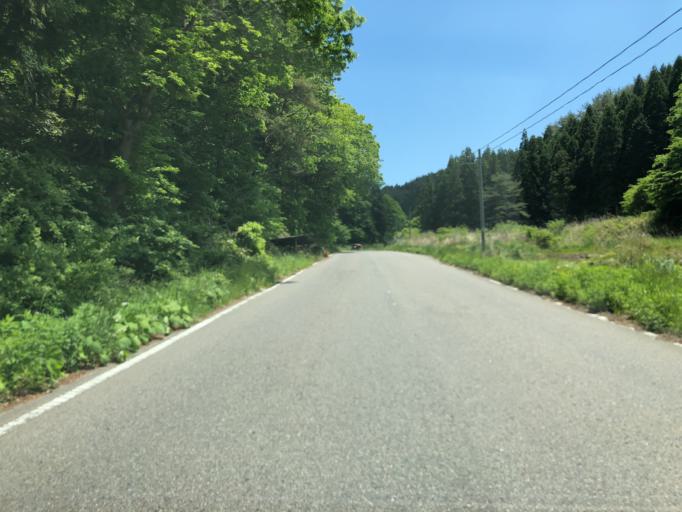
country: JP
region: Fukushima
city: Funehikimachi-funehiki
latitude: 37.5133
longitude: 140.6898
